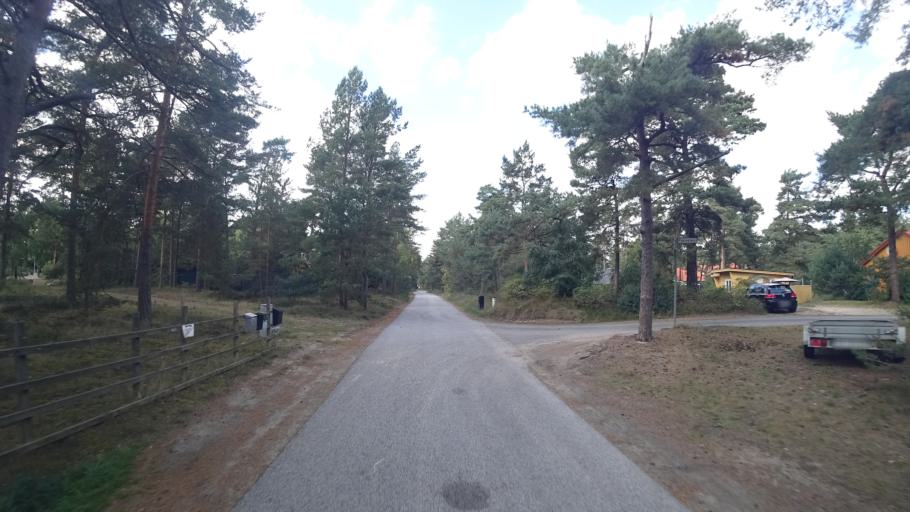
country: SE
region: Skane
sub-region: Kristianstads Kommun
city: Ahus
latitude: 55.9138
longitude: 14.2881
